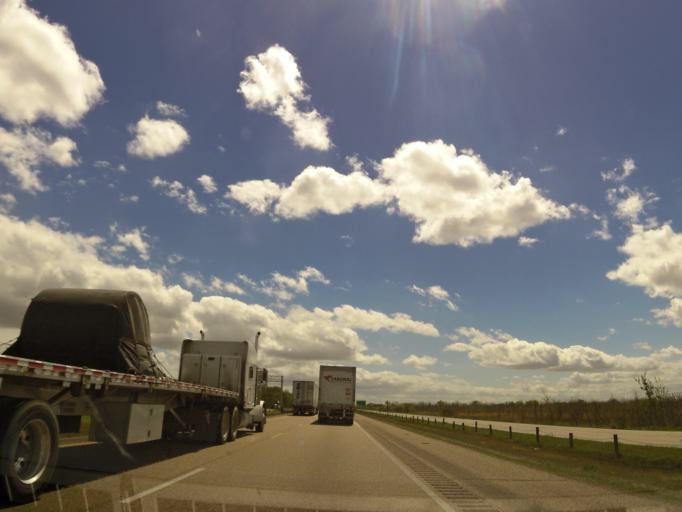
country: US
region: Arkansas
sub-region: Crittenden County
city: Marion
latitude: 35.3838
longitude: -90.2795
